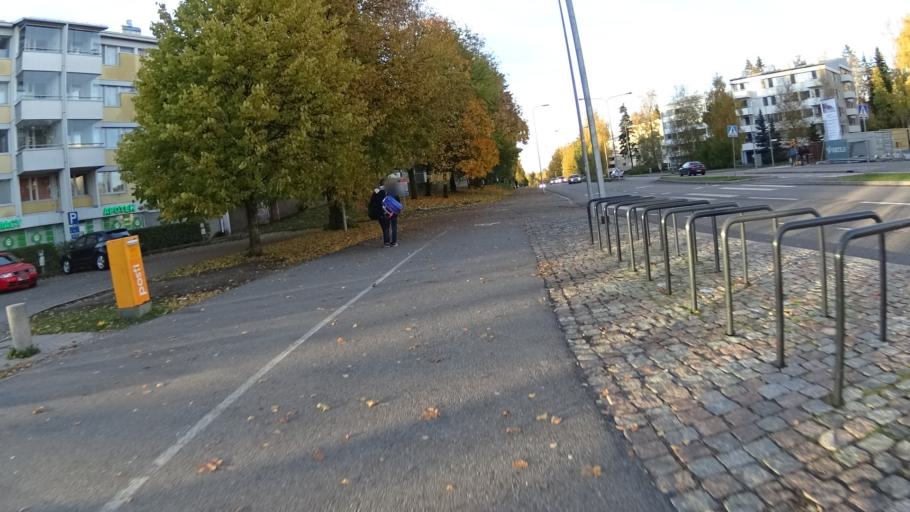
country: FI
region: Uusimaa
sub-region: Helsinki
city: Helsinki
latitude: 60.2317
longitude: 24.9336
